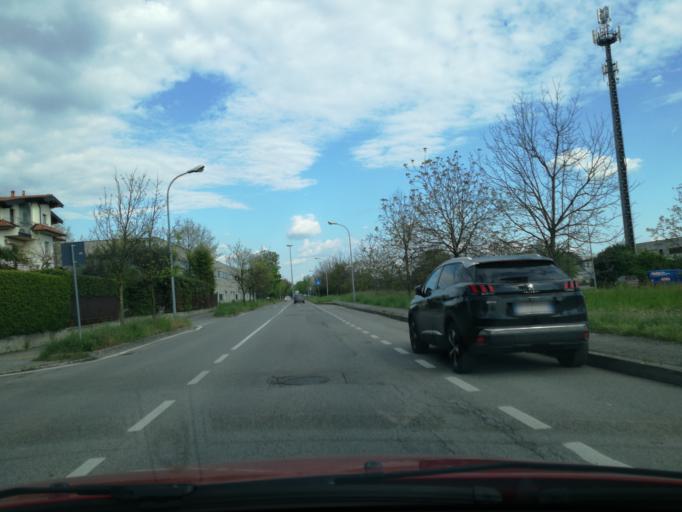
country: IT
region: Lombardy
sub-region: Provincia di Monza e Brianza
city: Seregno
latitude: 45.6552
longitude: 9.2189
